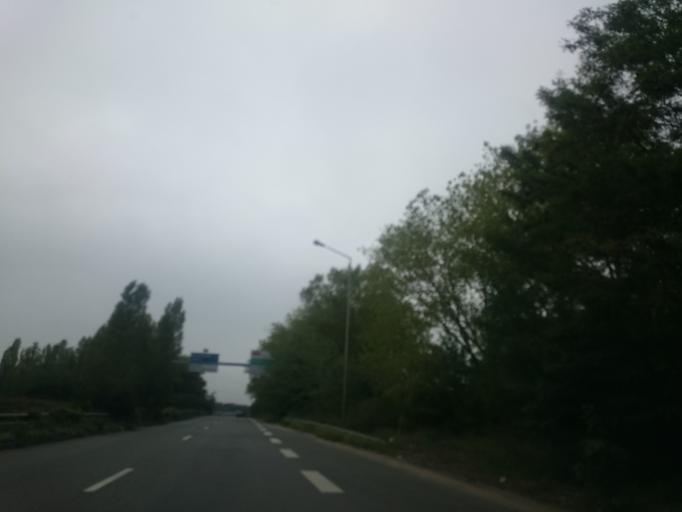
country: FR
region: Ile-de-France
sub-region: Departement de l'Essonne
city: Ris-Orangis
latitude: 48.6349
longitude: 2.4088
